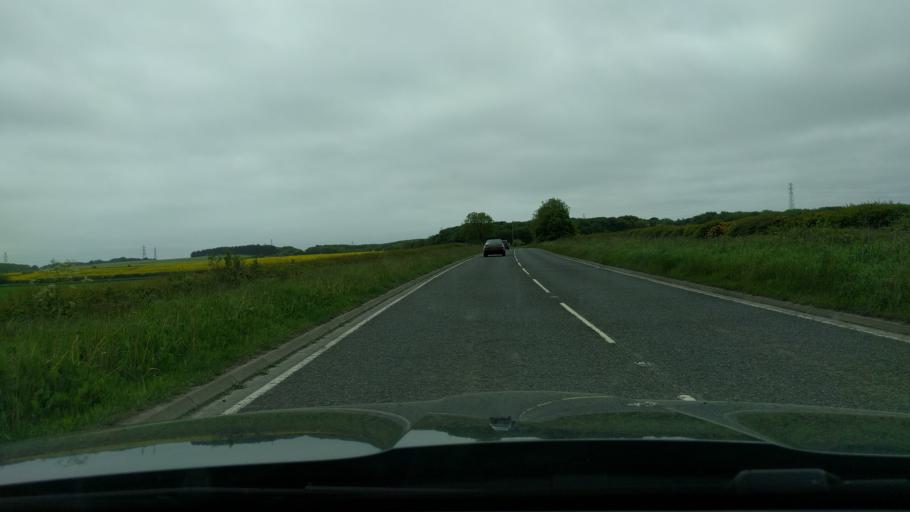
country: GB
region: England
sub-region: Northumberland
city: Cresswell
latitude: 55.2014
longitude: -1.5593
